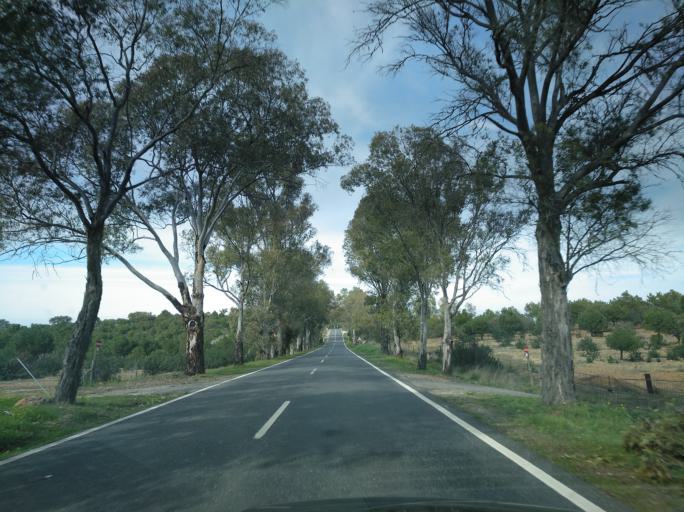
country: PT
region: Beja
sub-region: Mertola
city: Mertola
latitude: 37.7136
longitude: -7.7548
